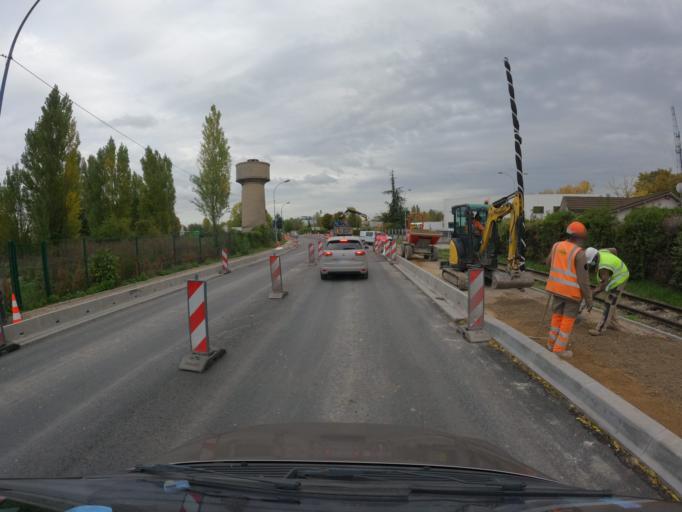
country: FR
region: Ile-de-France
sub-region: Departement de Seine-et-Marne
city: Chelles
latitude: 48.8697
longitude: 2.6077
